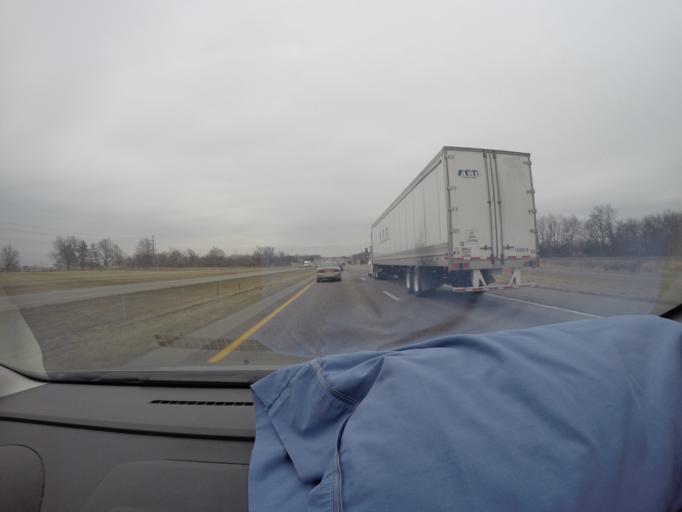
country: US
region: Missouri
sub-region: Saint Charles County
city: Wentzville
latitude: 38.8076
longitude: -90.9180
